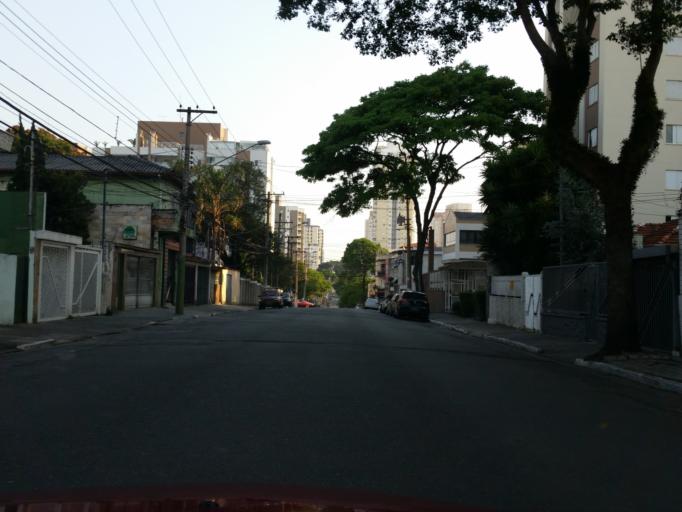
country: BR
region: Sao Paulo
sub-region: Sao Paulo
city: Sao Paulo
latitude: -23.6049
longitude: -46.6172
